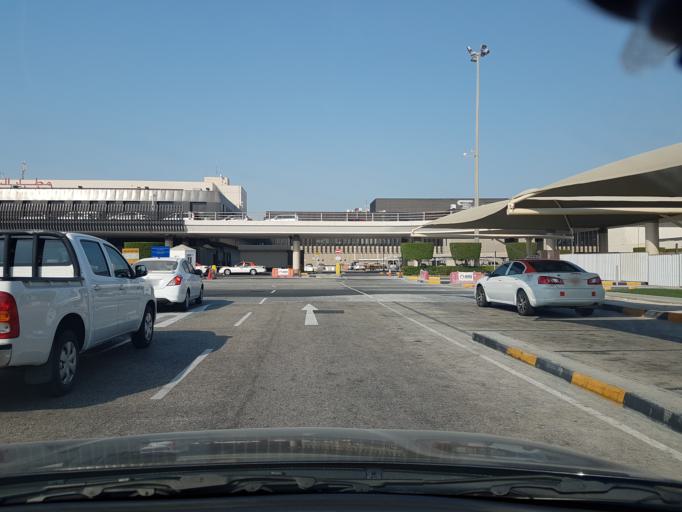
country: BH
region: Muharraq
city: Al Muharraq
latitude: 26.2683
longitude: 50.6262
